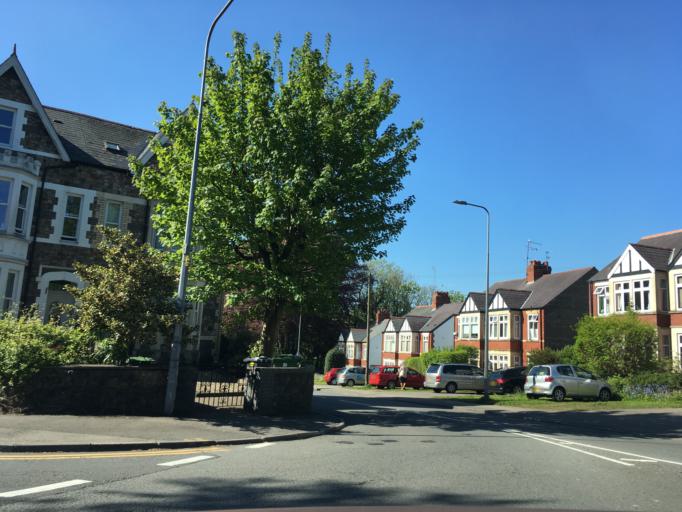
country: GB
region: Wales
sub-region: Cardiff
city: Radyr
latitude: 51.4966
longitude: -3.2234
